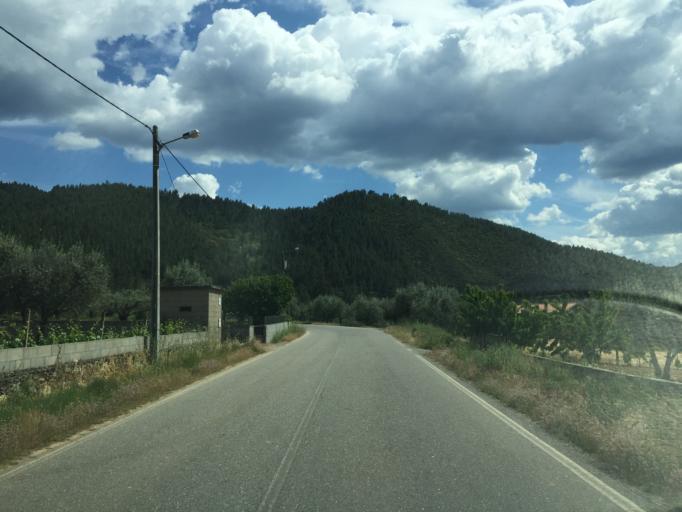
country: PT
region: Coimbra
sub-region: Pampilhosa da Serra
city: Pampilhosa da Serra
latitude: 40.0620
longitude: -7.7986
